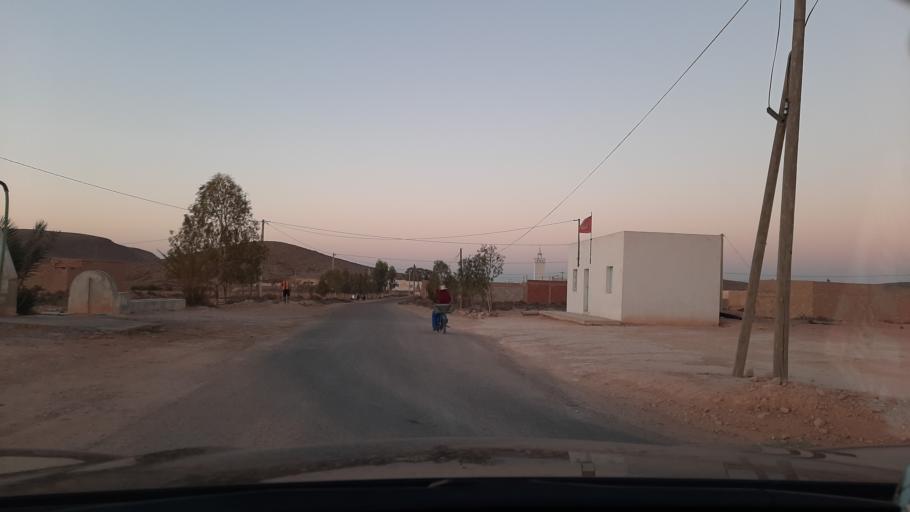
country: TN
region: Qabis
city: Matmata
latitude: 33.5690
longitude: 10.1768
